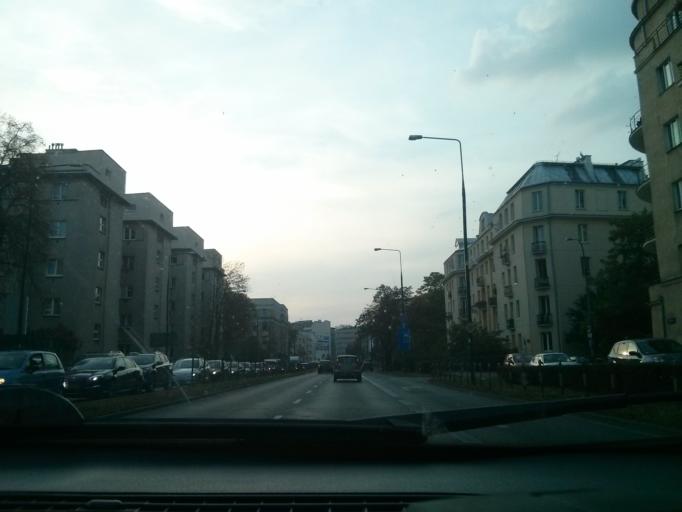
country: PL
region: Masovian Voivodeship
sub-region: Warszawa
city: Ochota
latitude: 52.2163
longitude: 20.9866
